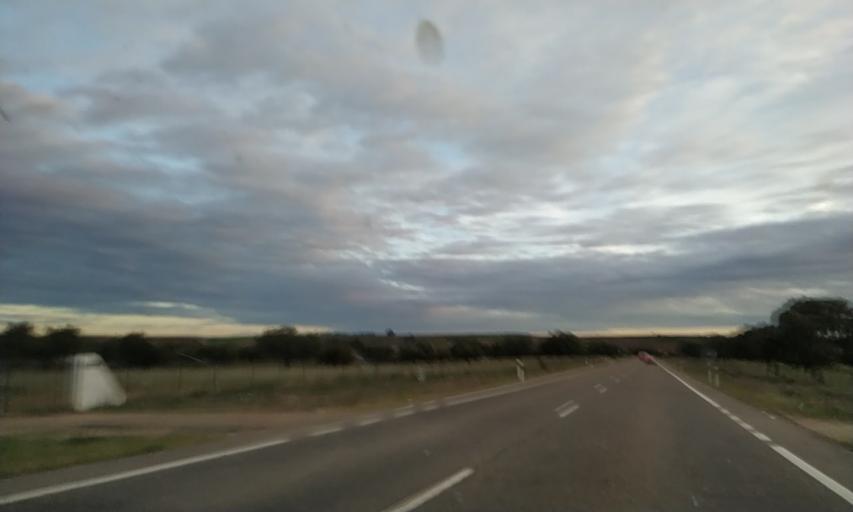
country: ES
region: Extremadura
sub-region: Provincia de Badajoz
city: La Roca de la Sierra
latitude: 39.1005
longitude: -6.7119
